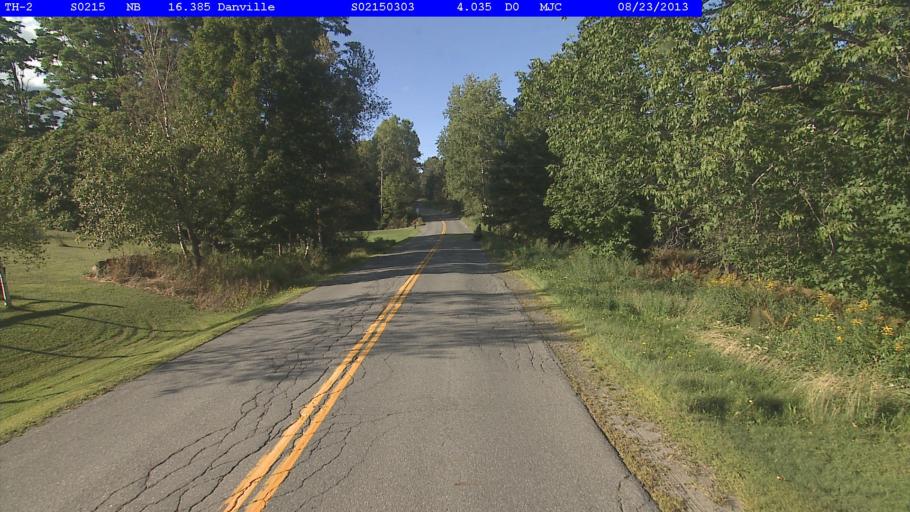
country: US
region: Vermont
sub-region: Caledonia County
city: St Johnsbury
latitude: 44.4221
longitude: -72.1421
